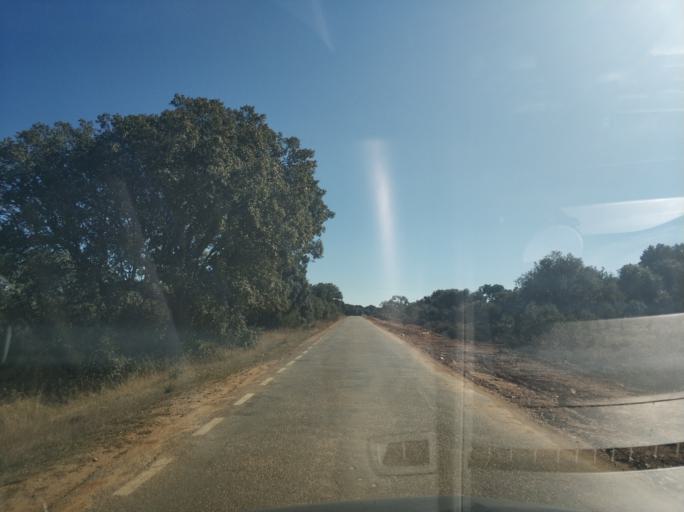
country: ES
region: Castille and Leon
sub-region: Provincia de Salamanca
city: Doninos de Salamanca
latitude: 40.9300
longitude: -5.7417
